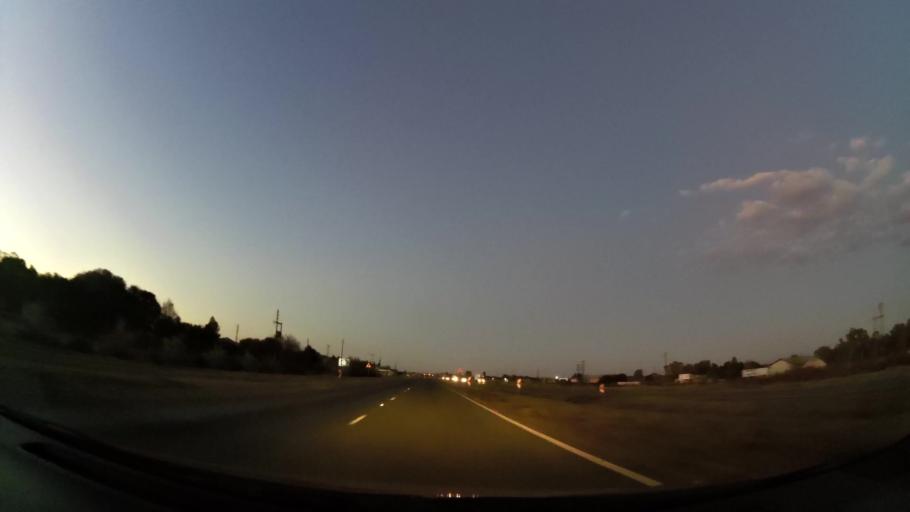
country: ZA
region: North-West
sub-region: Dr Kenneth Kaunda District Municipality
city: Potchefstroom
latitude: -26.6974
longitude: 27.1324
